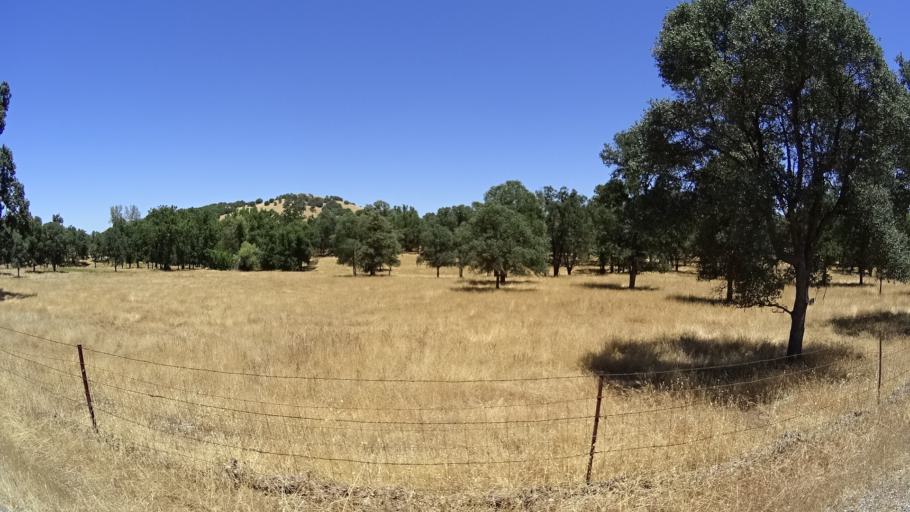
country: US
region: California
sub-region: Calaveras County
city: Copperopolis
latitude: 38.0720
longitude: -120.6629
